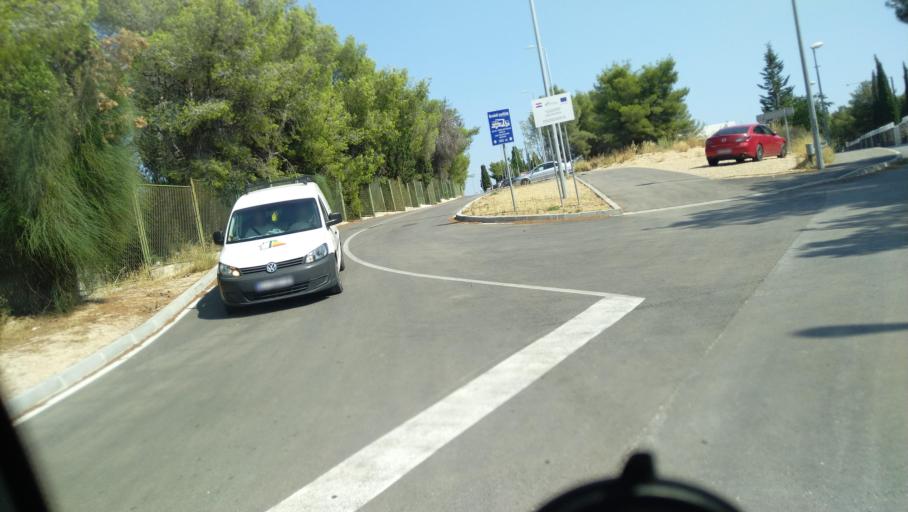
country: HR
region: Sibensko-Kniniska
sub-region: Grad Sibenik
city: Sibenik
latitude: 43.7176
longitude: 15.9065
